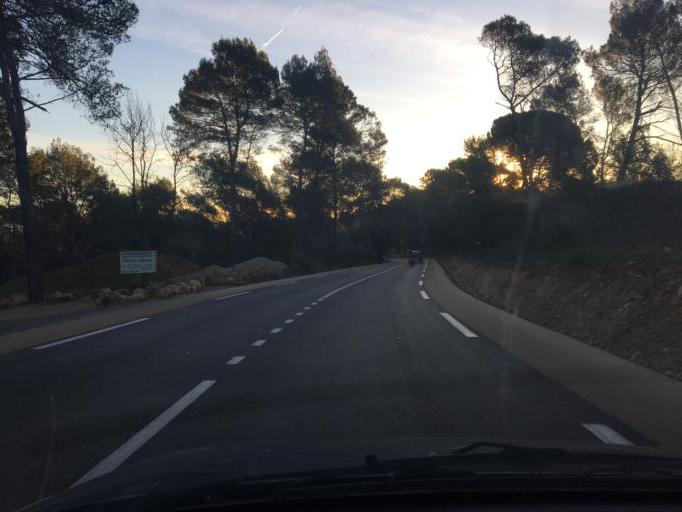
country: FR
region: Provence-Alpes-Cote d'Azur
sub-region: Departement du Var
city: Taradeau
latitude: 43.4613
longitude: 6.4064
